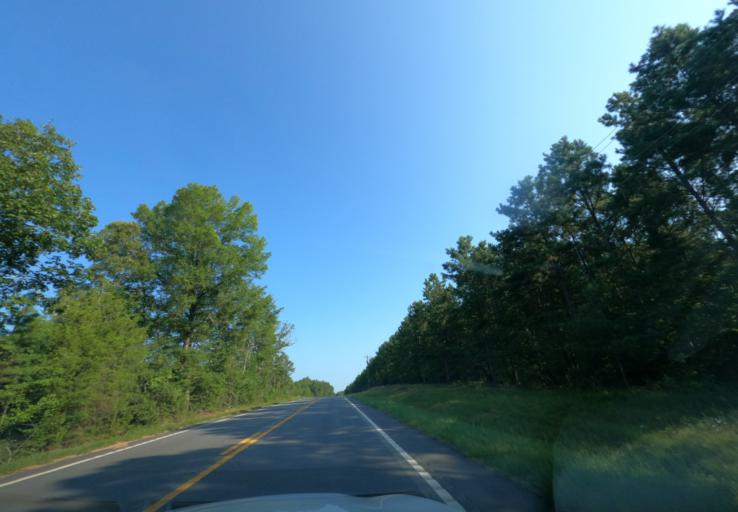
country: US
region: South Carolina
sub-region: Edgefield County
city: Edgefield
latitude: 33.8415
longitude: -81.9746
